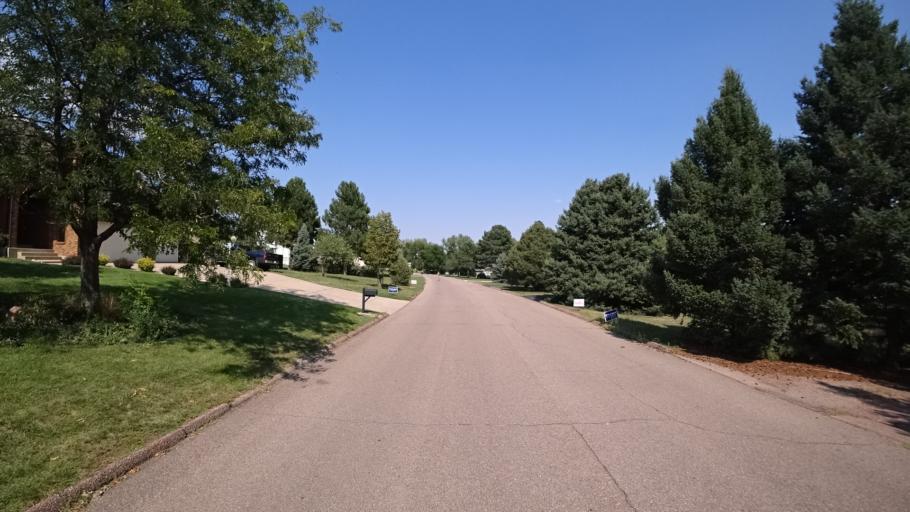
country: US
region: Colorado
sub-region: El Paso County
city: Colorado Springs
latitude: 38.7980
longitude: -104.8256
